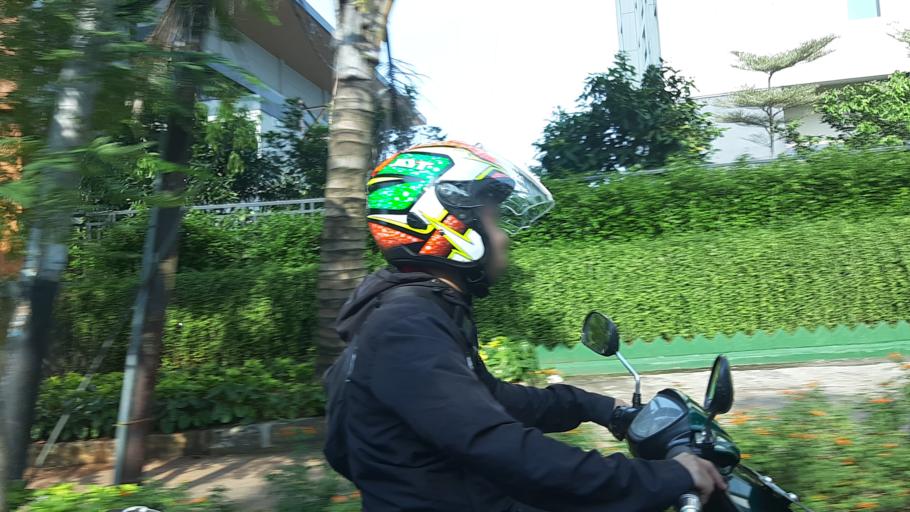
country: ID
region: Jakarta Raya
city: Jakarta
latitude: -6.1731
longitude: 106.7658
